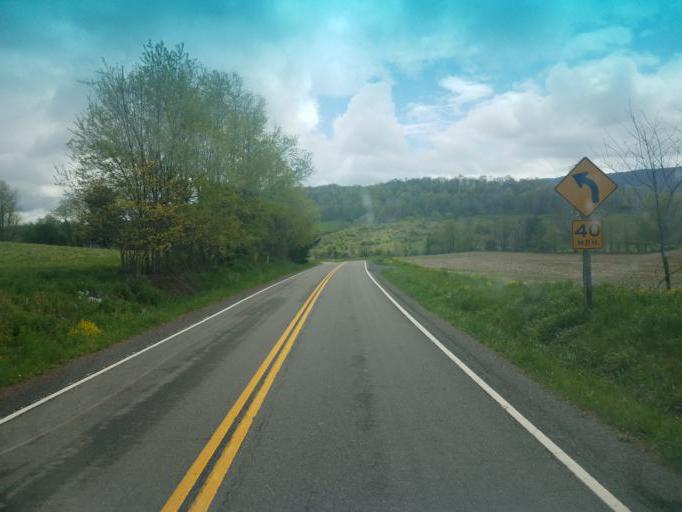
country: US
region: Virginia
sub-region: Wythe County
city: Rural Retreat
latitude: 37.0072
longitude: -81.3647
